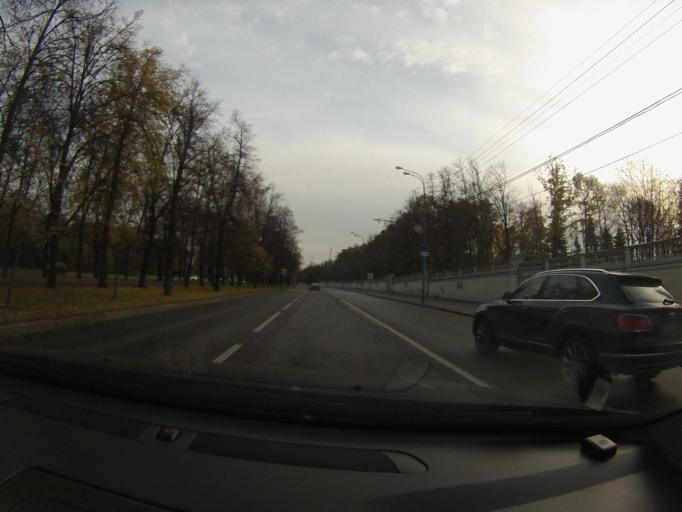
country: RU
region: Moscow
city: Vorob'yovo
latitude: 55.7192
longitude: 37.5349
